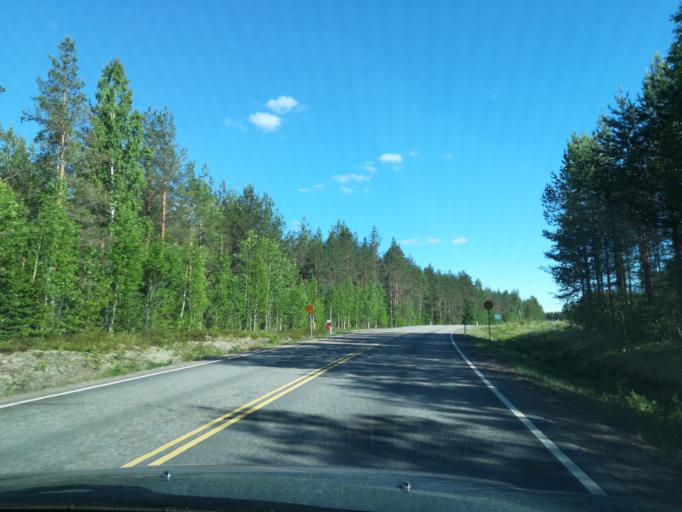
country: FI
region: South Karelia
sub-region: Imatra
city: Ruokolahti
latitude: 61.3972
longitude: 28.6329
